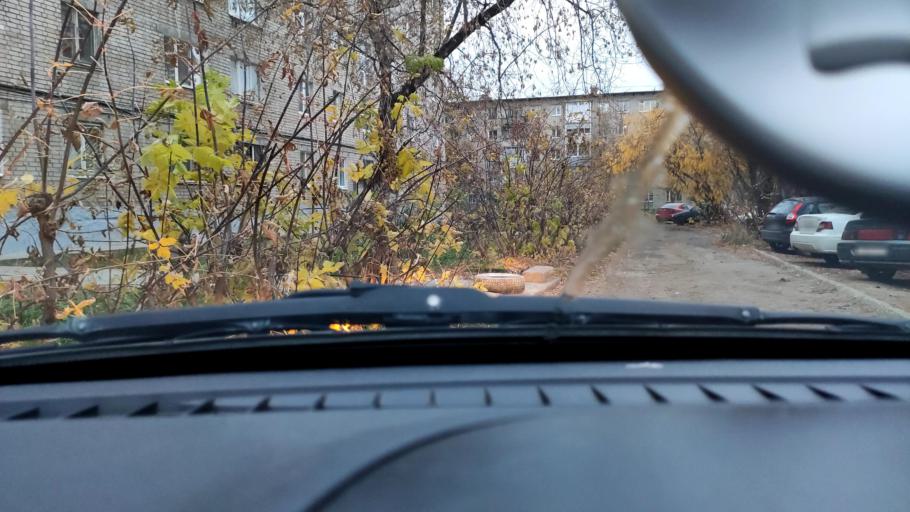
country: RU
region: Perm
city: Kondratovo
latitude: 57.9632
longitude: 56.1721
